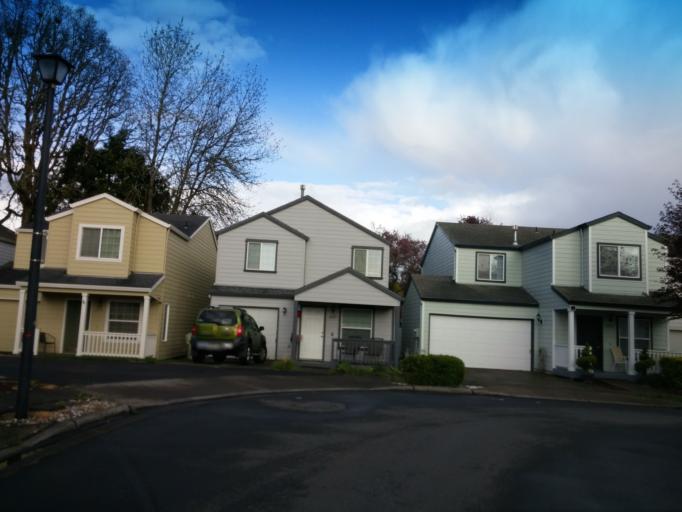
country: US
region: Oregon
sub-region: Washington County
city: Aloha
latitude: 45.5141
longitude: -122.8510
